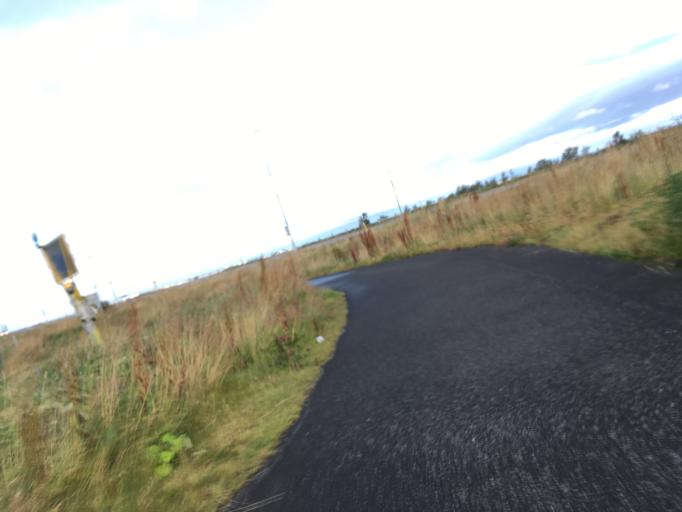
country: IS
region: Capital Region
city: Mosfellsbaer
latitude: 64.1583
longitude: -21.7244
